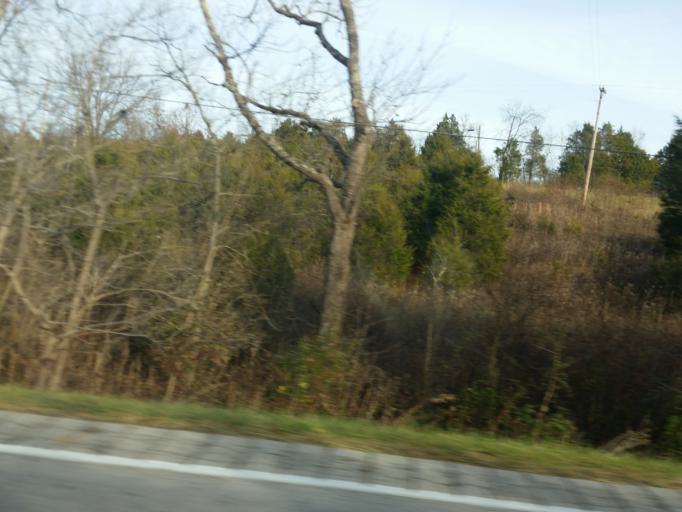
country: US
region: Kentucky
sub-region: Harrison County
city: Cynthiana
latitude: 38.5036
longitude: -84.2929
